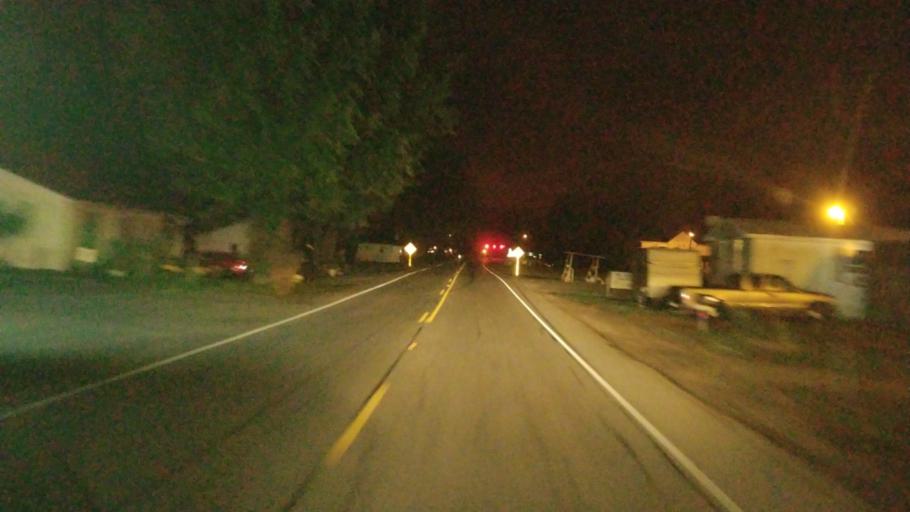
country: US
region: Ohio
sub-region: Pike County
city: Piketon
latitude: 39.0503
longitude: -83.0510
